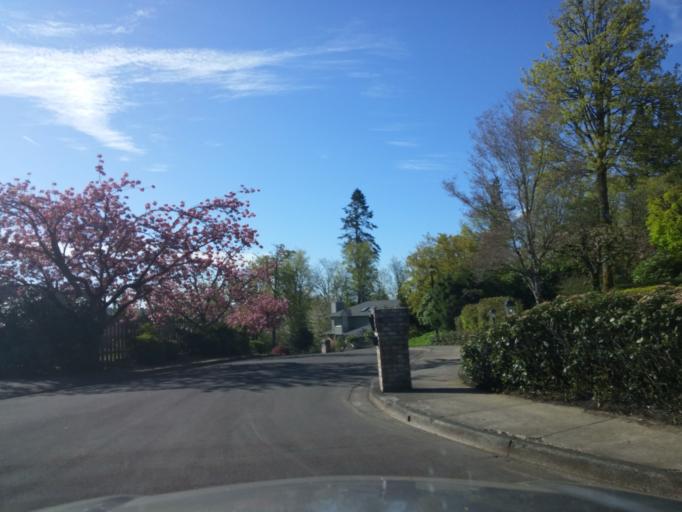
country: US
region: Oregon
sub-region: Washington County
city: Cedar Mill
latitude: 45.5351
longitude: -122.7883
